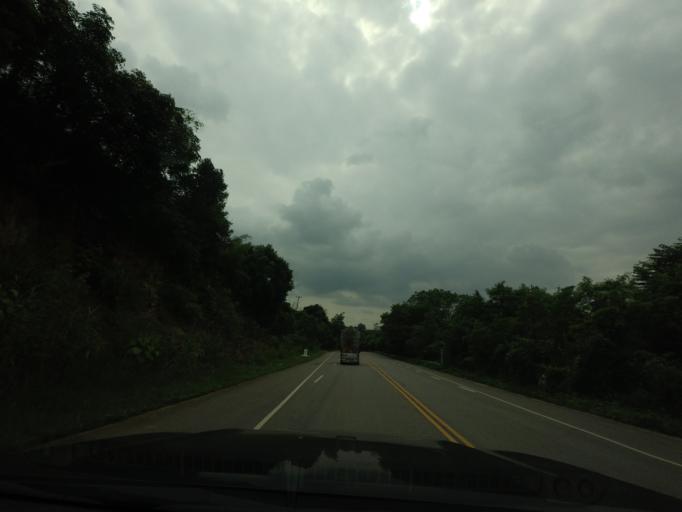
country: TH
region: Loei
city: Dan Sai
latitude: 17.2108
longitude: 101.1660
